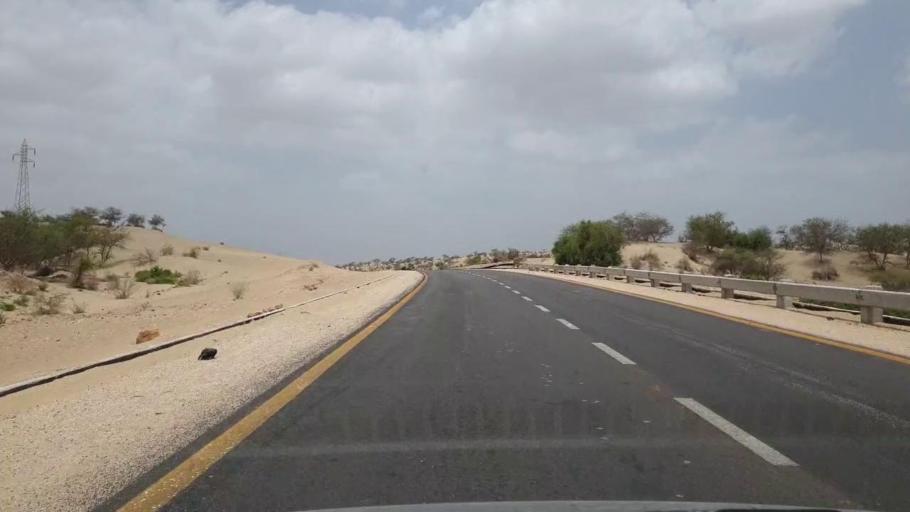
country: PK
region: Sindh
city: Naukot
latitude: 24.8470
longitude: 69.5244
